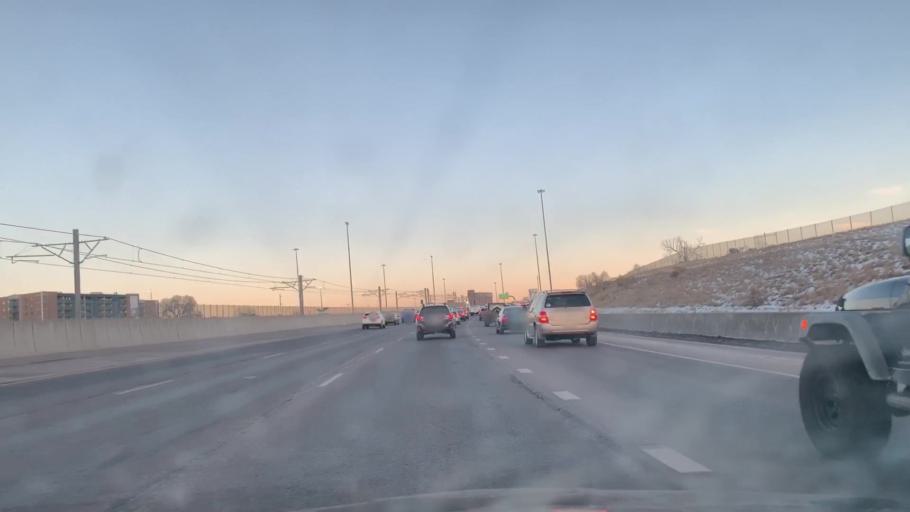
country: US
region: Colorado
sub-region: Adams County
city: Aurora
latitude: 39.6542
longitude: -104.8523
